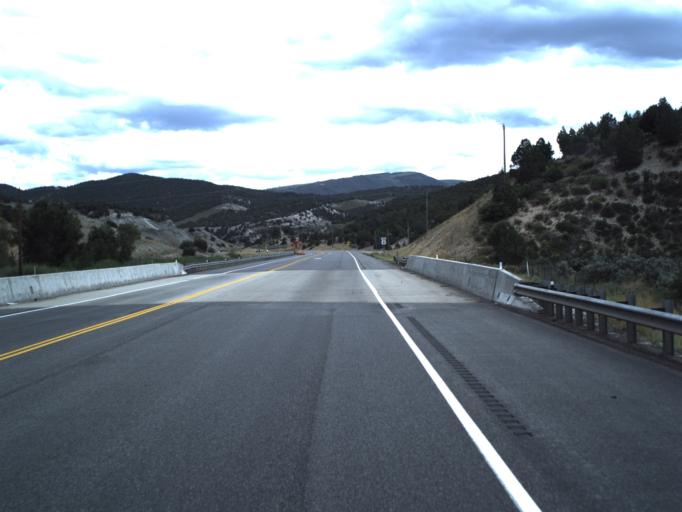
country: US
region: Utah
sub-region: Sanpete County
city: Fairview
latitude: 39.9494
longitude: -111.2174
